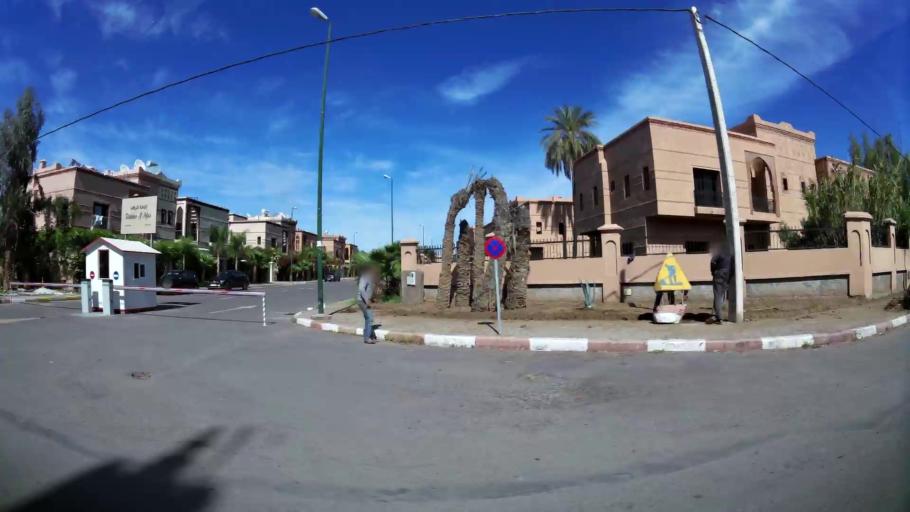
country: MA
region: Marrakech-Tensift-Al Haouz
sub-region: Marrakech
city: Marrakesh
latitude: 31.6574
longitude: -8.0537
